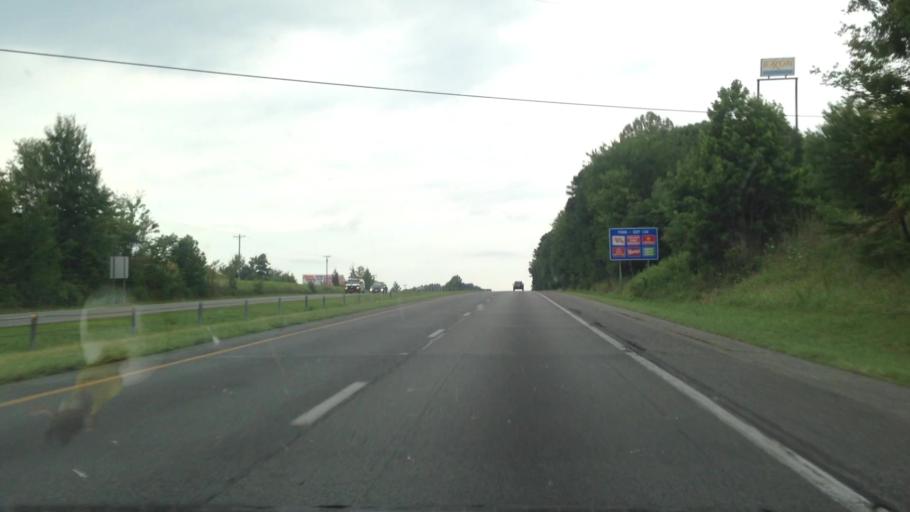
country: US
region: North Carolina
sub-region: Surry County
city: Pilot Mountain
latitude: 36.3672
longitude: -80.4824
